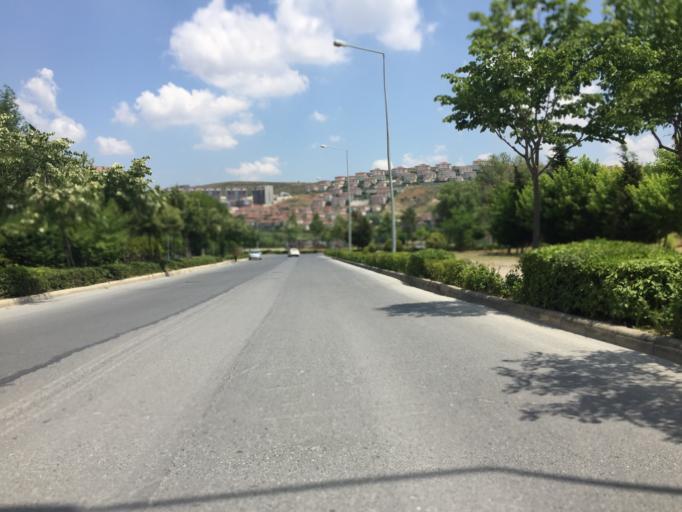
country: TR
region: Istanbul
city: Esenyurt
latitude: 41.0850
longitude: 28.6709
